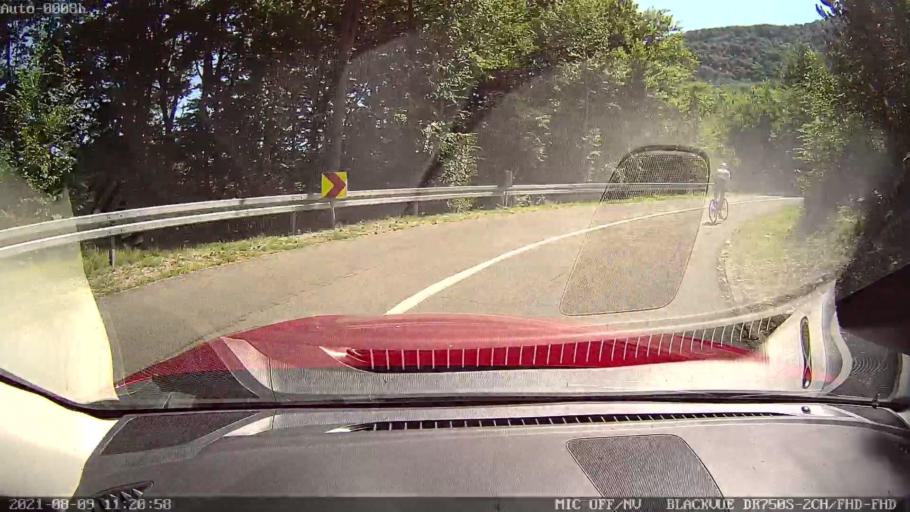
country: HR
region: Istarska
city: Lovran
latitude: 45.3038
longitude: 14.1980
